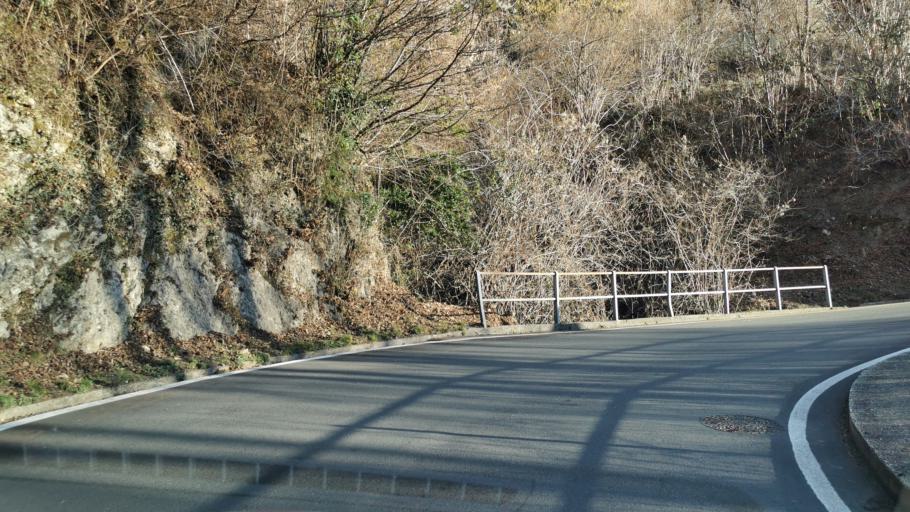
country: IT
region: Lombardy
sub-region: Provincia di Como
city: Plesio
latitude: 46.0498
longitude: 9.2294
